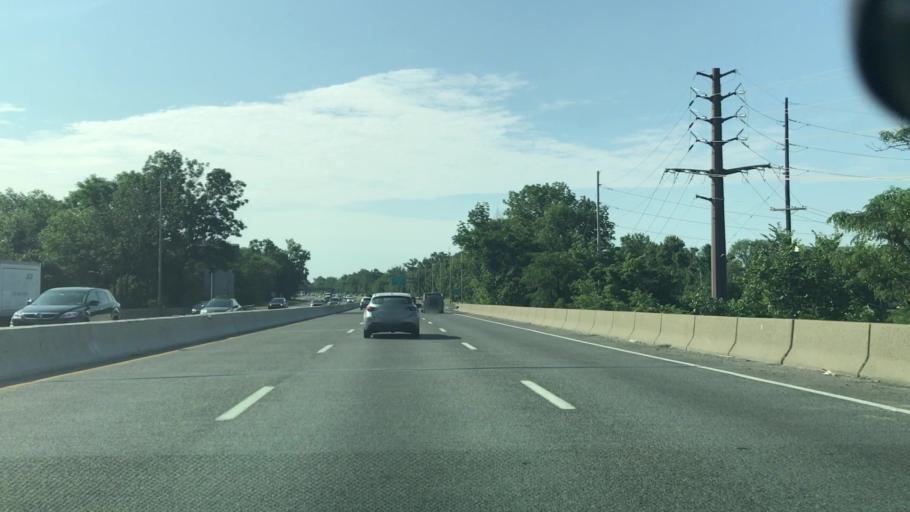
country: US
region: New Jersey
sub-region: Somerset County
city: South Bound Brook
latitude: 40.5540
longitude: -74.5444
